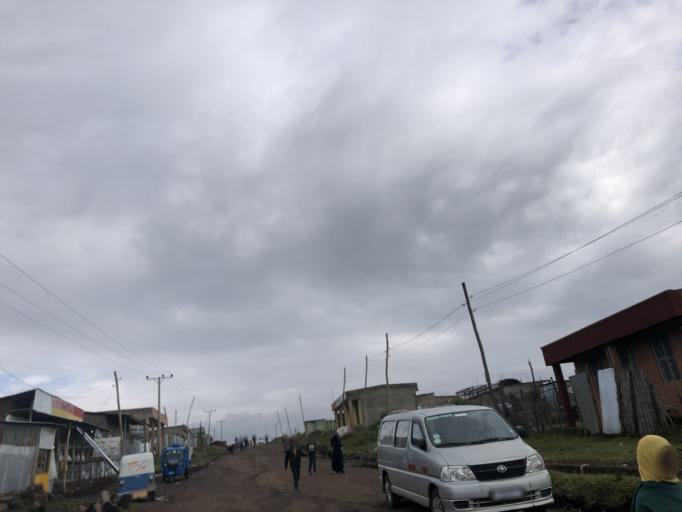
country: ET
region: Southern Nations, Nationalities, and People's Region
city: Butajira
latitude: 7.8340
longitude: 38.1788
